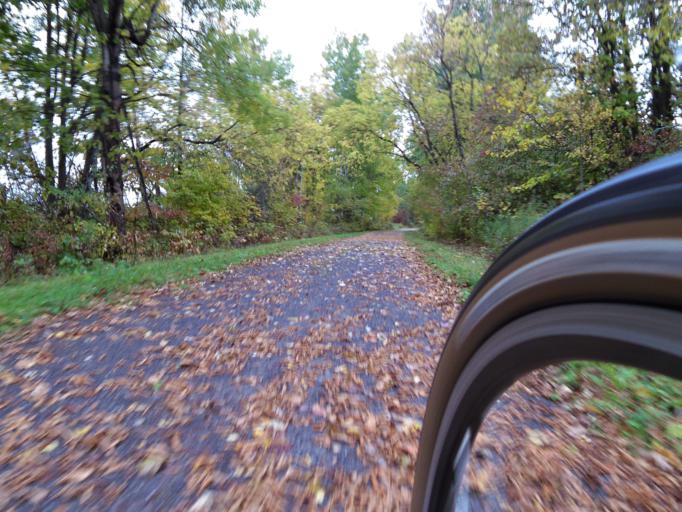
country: CA
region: Quebec
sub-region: Outaouais
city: Shawville
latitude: 45.6992
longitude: -76.5806
